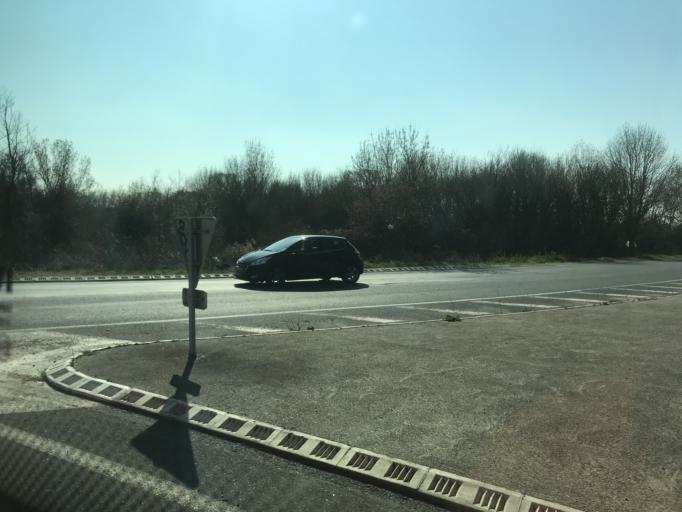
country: FR
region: Languedoc-Roussillon
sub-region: Departement de l'Herault
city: Perols
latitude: 43.5798
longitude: 3.9441
